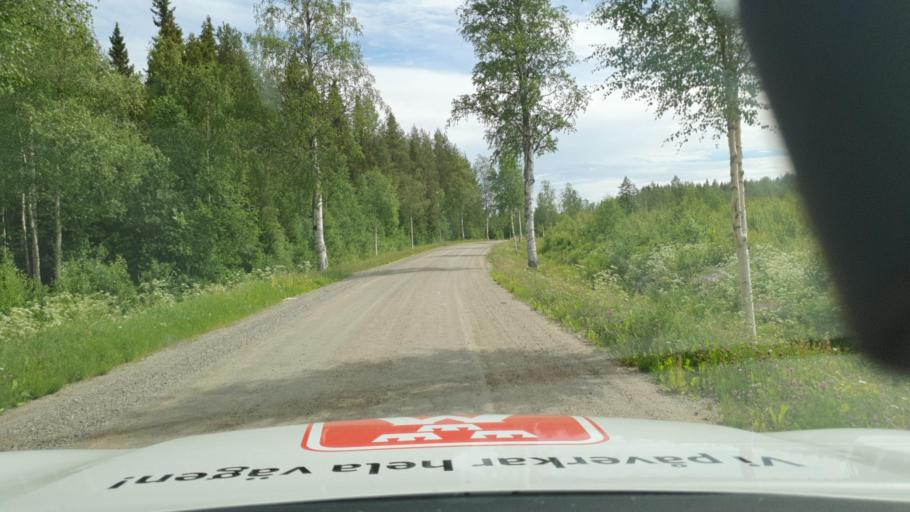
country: SE
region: Vaesterbotten
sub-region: Skelleftea Kommun
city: Burtraesk
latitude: 64.4691
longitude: 20.4581
